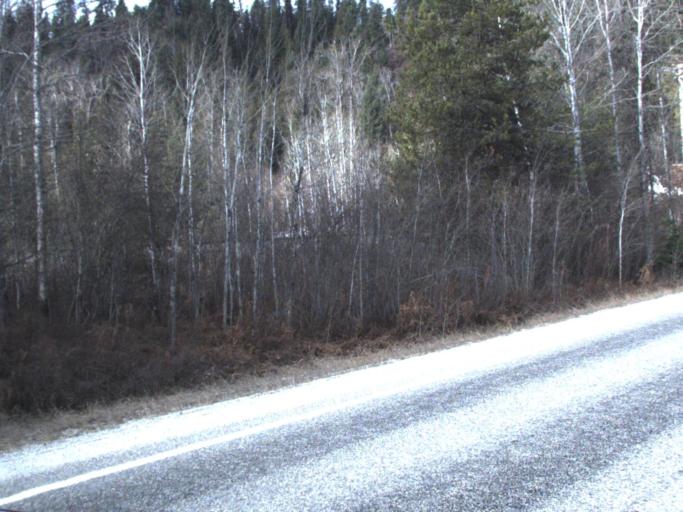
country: US
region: Washington
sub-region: Stevens County
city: Chewelah
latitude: 48.5510
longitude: -117.3377
